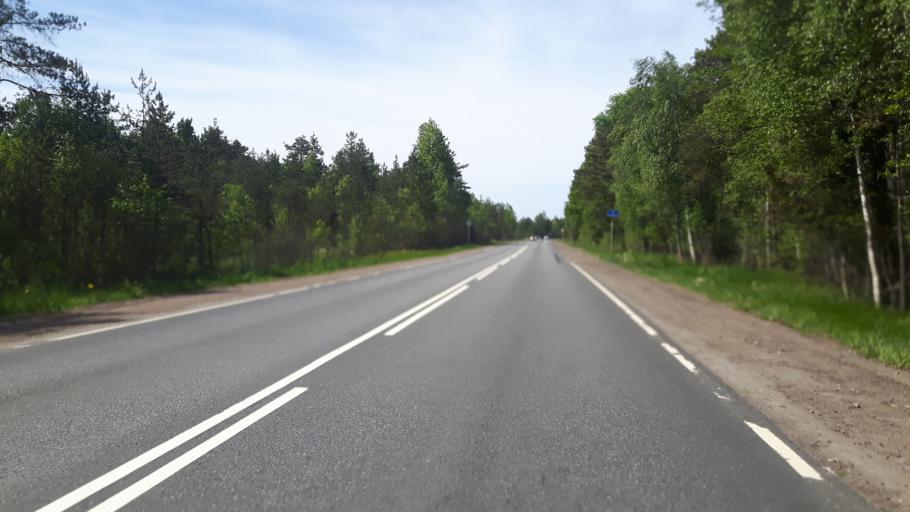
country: RU
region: Leningrad
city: Ust'-Luga
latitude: 59.6601
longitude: 28.4121
